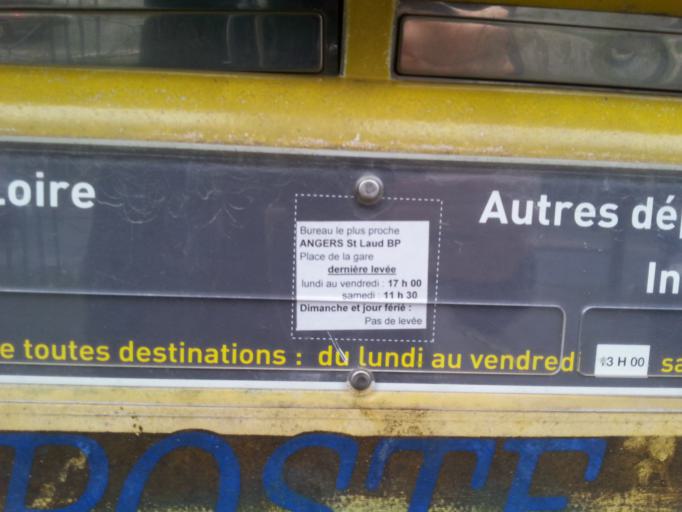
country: FR
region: Pays de la Loire
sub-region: Departement de Maine-et-Loire
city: Angers
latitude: 47.4668
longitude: -0.5543
